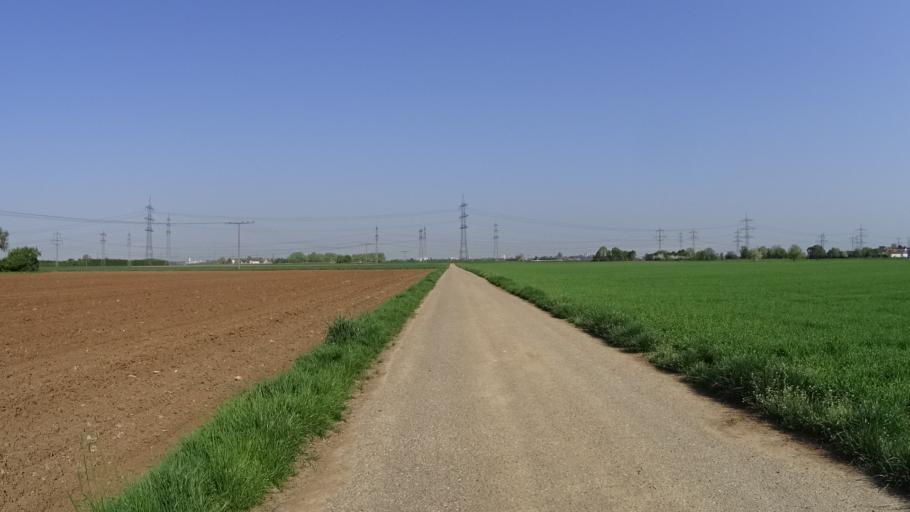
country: DE
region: Baden-Wuerttemberg
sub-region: Karlsruhe Region
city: Heddesheim
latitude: 49.5043
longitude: 8.5898
